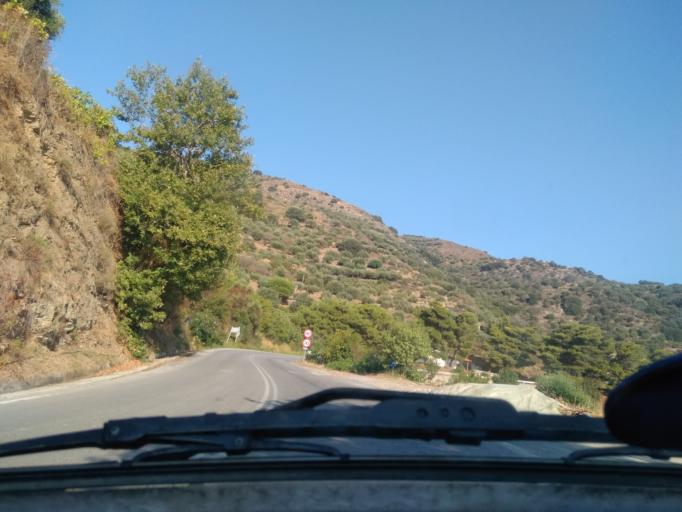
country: GR
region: Crete
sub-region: Nomos Lasithiou
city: Makry-Gialos
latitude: 35.1611
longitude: 25.9703
